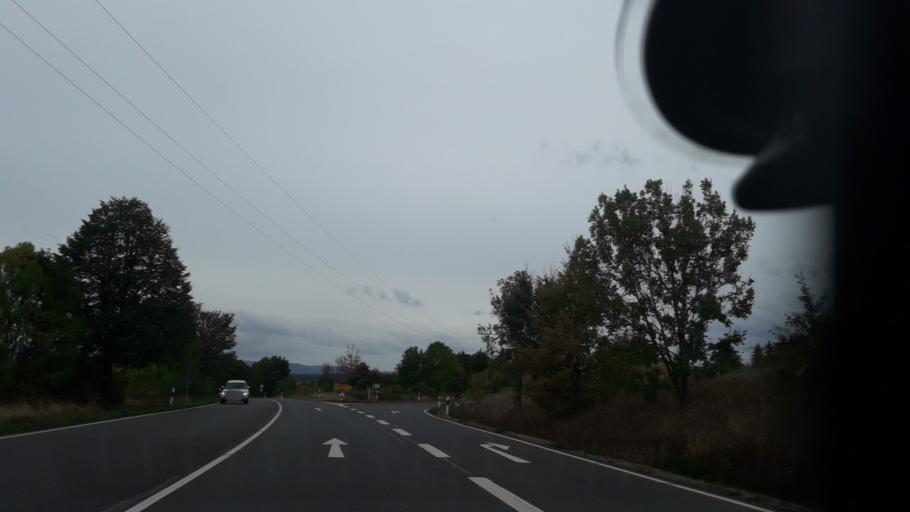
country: DE
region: Lower Saxony
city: Werlaburgdorf
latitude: 52.0540
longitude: 10.5430
